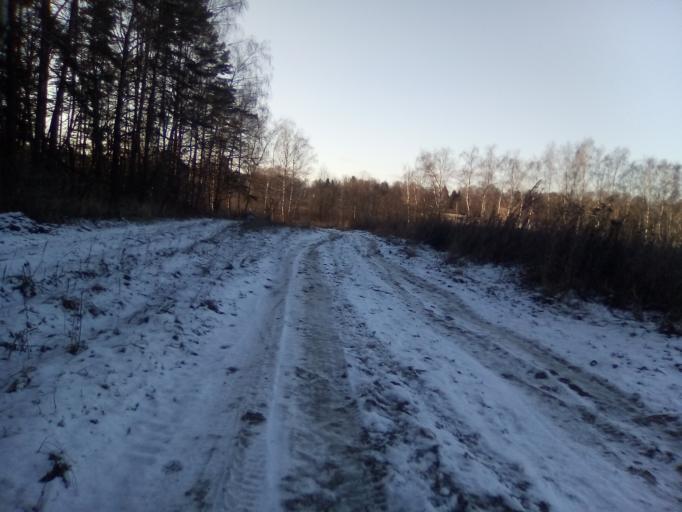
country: RU
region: Moskovskaya
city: Lesnoy Gorodok
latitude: 55.6493
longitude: 37.1761
